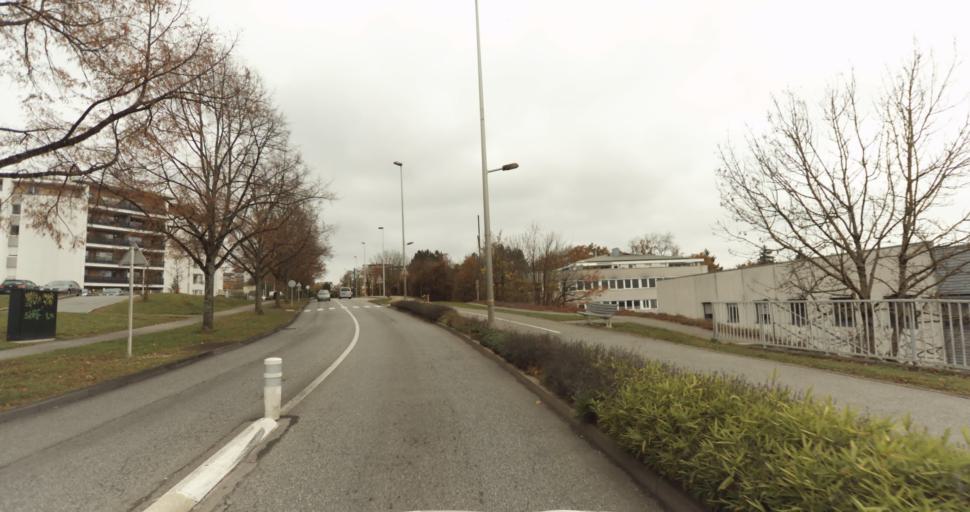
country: FR
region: Rhone-Alpes
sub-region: Departement de la Haute-Savoie
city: Cran-Gevrier
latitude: 45.8852
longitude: 6.1039
